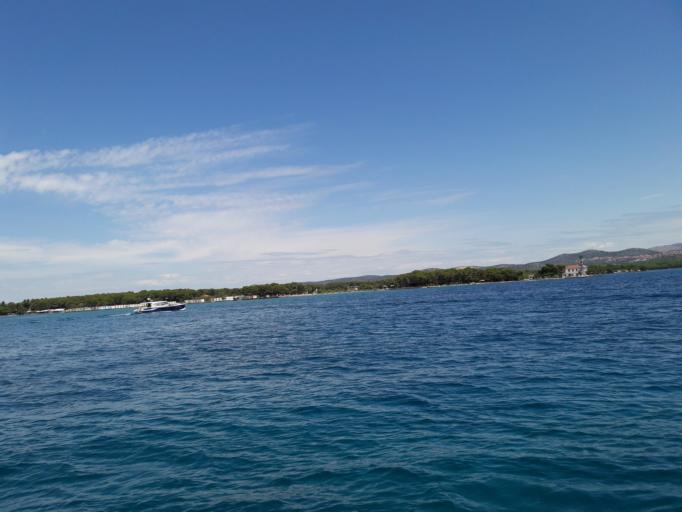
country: HR
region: Sibensko-Kniniska
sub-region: Grad Sibenik
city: Sibenik
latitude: 43.7182
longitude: 15.8463
